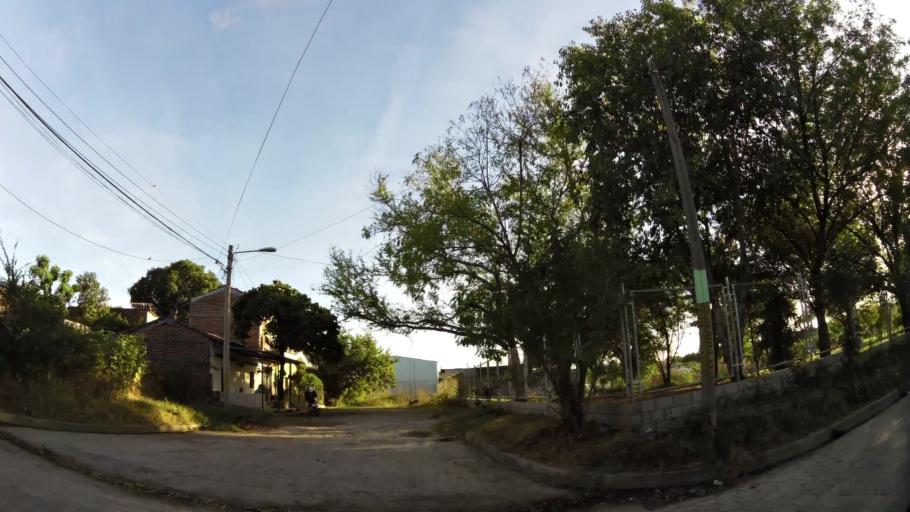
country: SV
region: San Miguel
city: San Miguel
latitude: 13.4588
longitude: -88.1663
